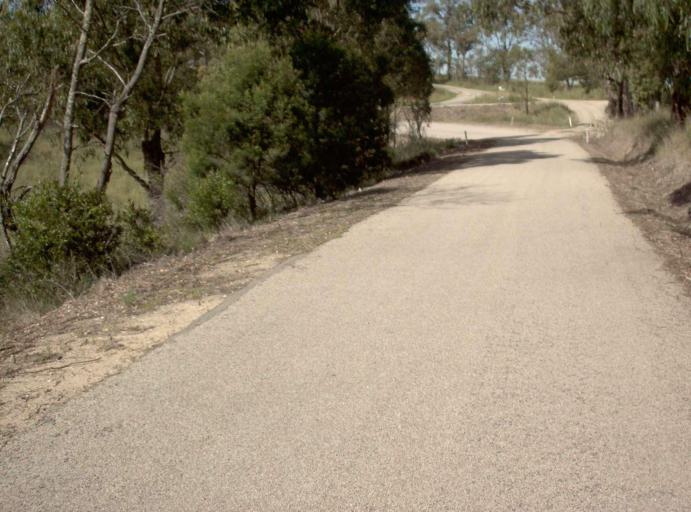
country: AU
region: Victoria
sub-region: East Gippsland
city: Lakes Entrance
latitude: -37.5206
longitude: 148.1403
